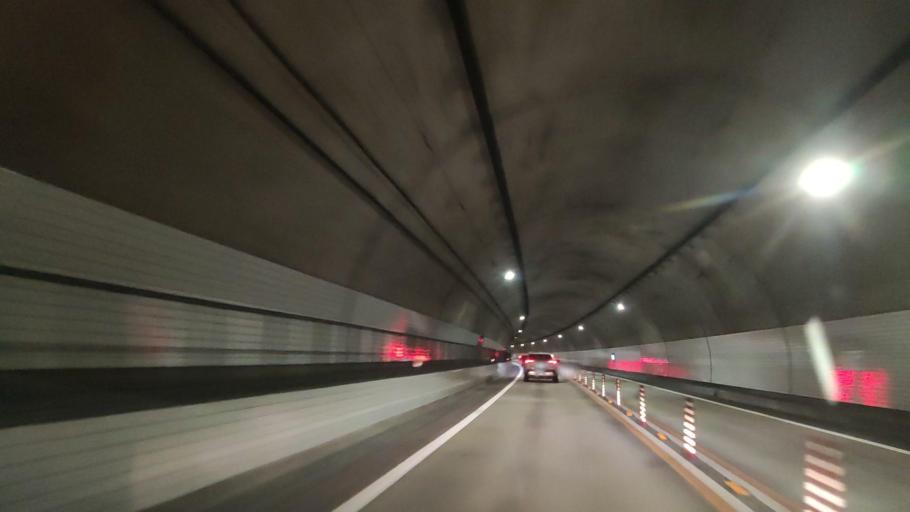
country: JP
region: Kyoto
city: Miyazu
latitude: 35.5595
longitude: 135.1234
